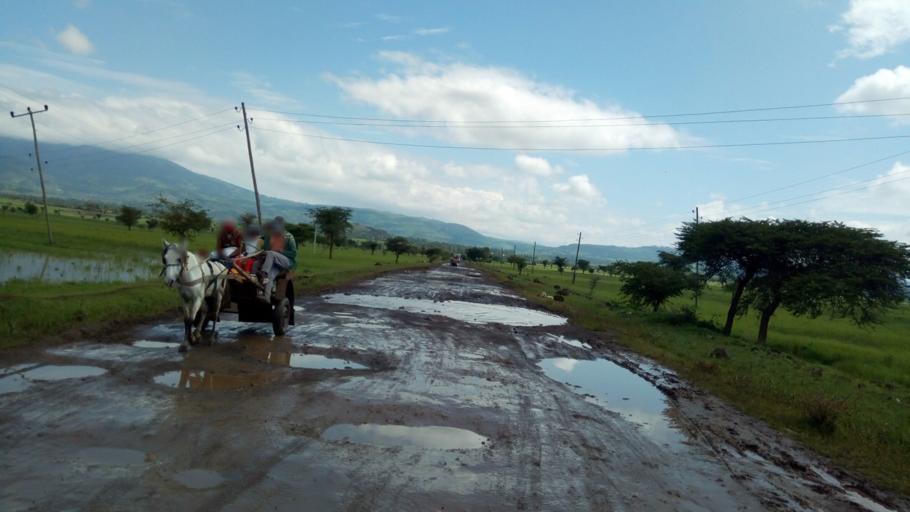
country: ET
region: Oromiya
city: Bishoftu
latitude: 8.8065
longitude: 39.0037
